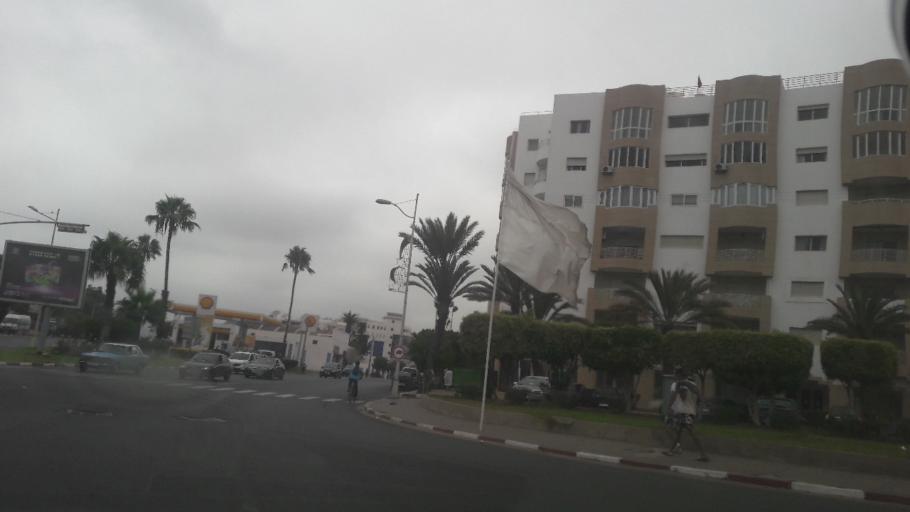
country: MA
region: Souss-Massa-Draa
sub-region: Agadir-Ida-ou-Tnan
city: Agadir
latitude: 30.4078
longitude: -9.5878
